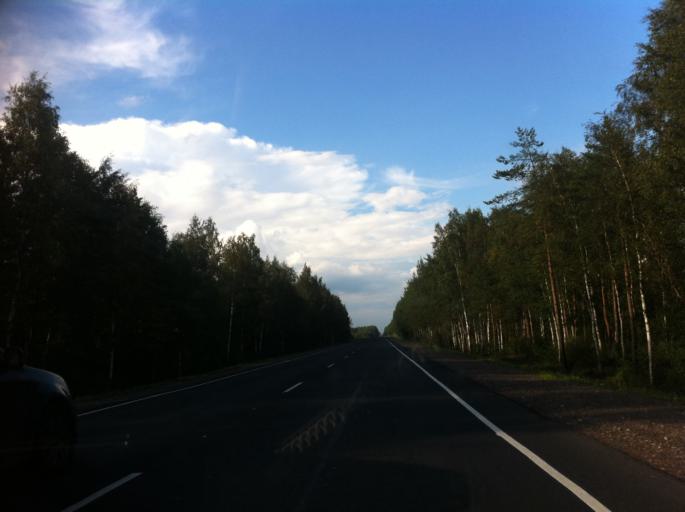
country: RU
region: Leningrad
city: Luga
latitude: 58.4453
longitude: 29.7547
